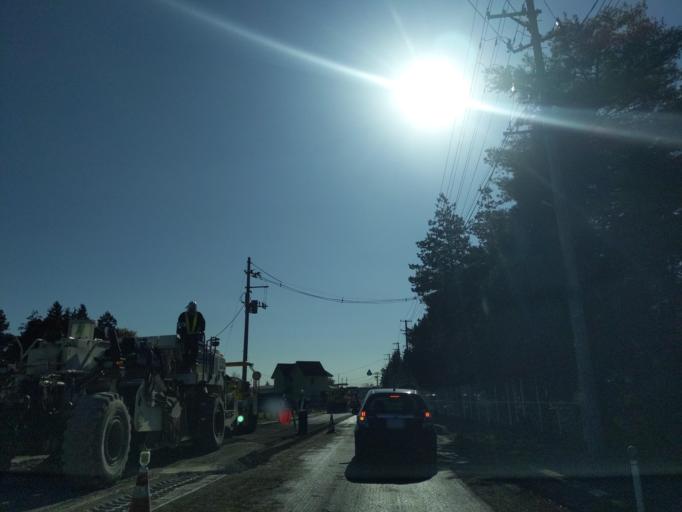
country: JP
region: Fukushima
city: Sukagawa
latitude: 37.3077
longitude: 140.3391
